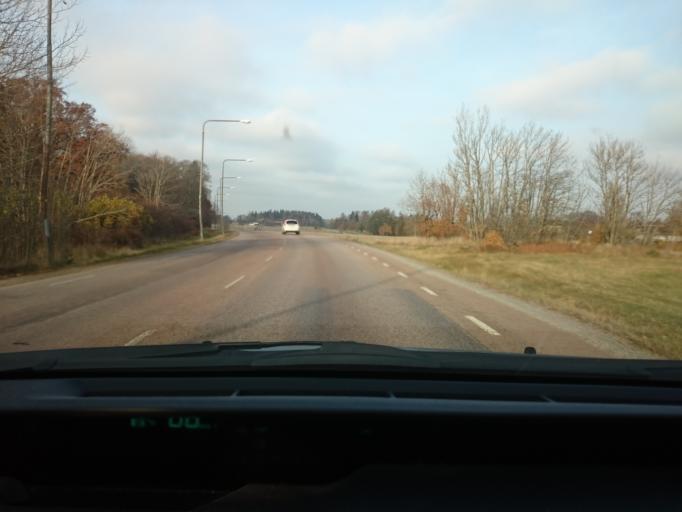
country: SE
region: Vaestmanland
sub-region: Vasteras
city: Vasteras
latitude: 59.6439
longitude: 16.5029
